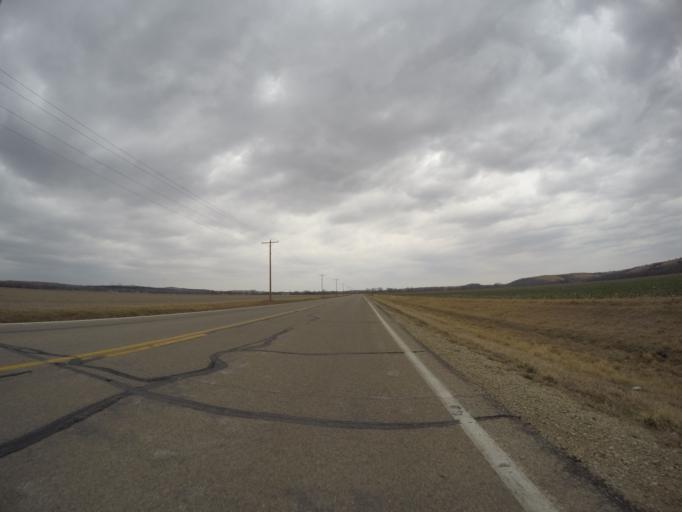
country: US
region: Kansas
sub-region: Riley County
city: Manhattan
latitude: 39.2280
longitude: -96.5632
